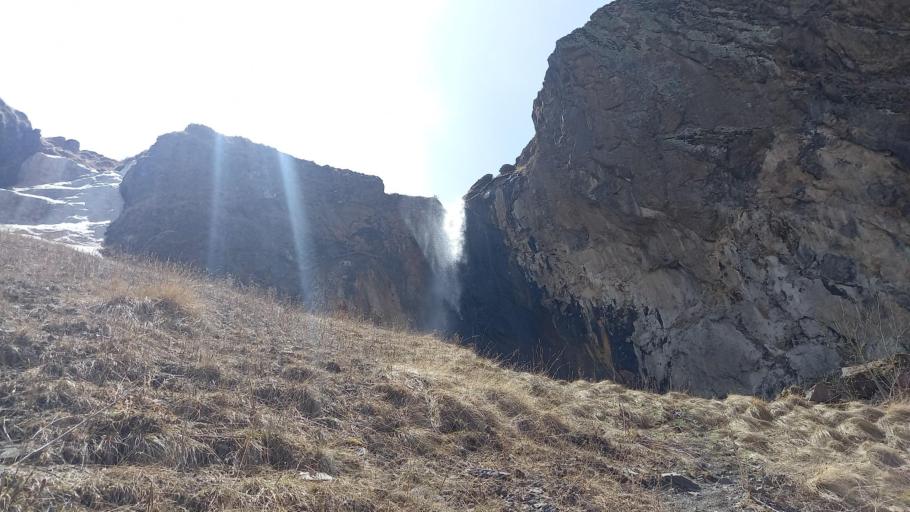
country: RU
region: Kabardino-Balkariya
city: Terskol
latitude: 43.4395
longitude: 42.5447
